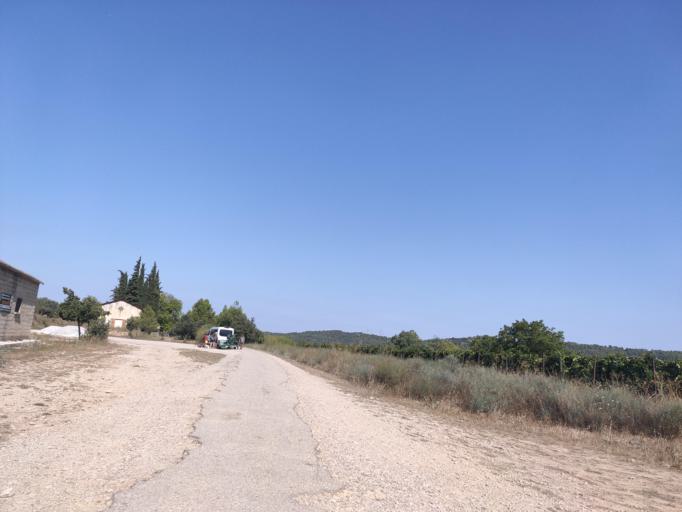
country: ES
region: Catalonia
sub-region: Provincia de Tarragona
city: Horta de Sant Joan
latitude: 40.9638
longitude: 0.3217
